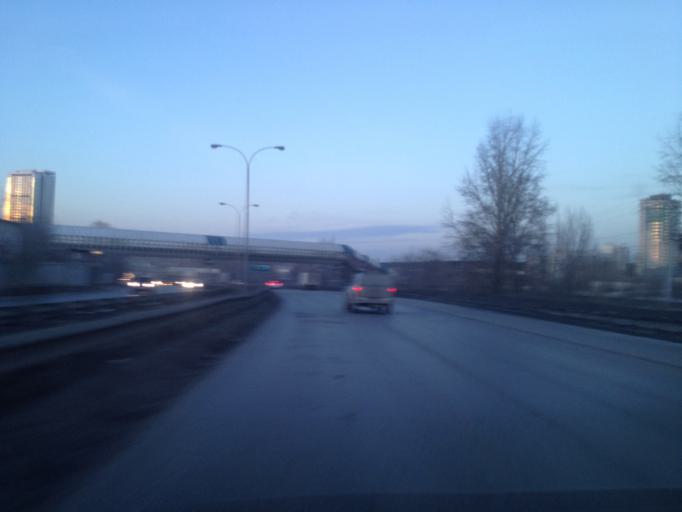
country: RU
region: Sverdlovsk
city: Yekaterinburg
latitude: 56.7912
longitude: 60.6383
